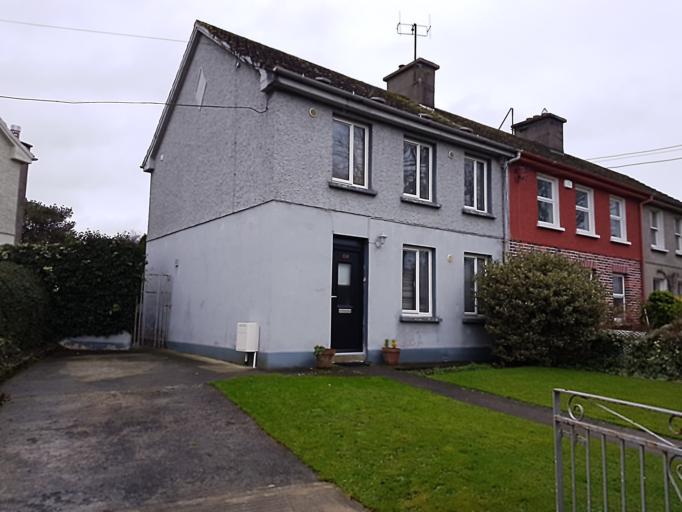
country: IE
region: Leinster
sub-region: Kilkenny
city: Kilkenny
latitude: 52.6561
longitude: -7.2387
